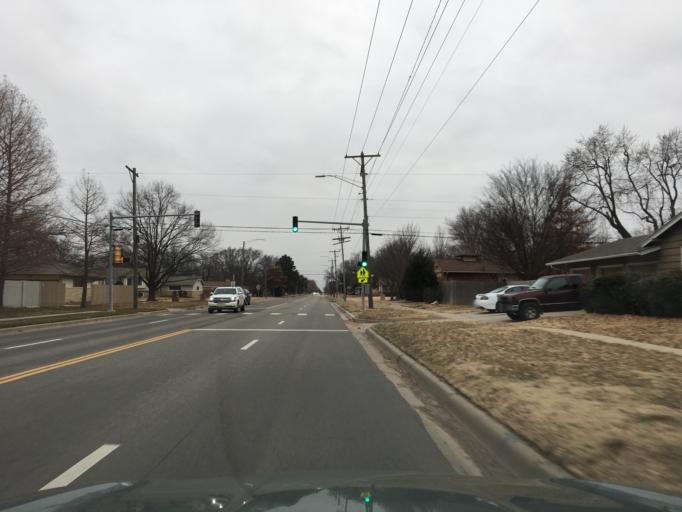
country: US
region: Kansas
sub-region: Sedgwick County
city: Bellaire
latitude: 37.7057
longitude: -97.2623
